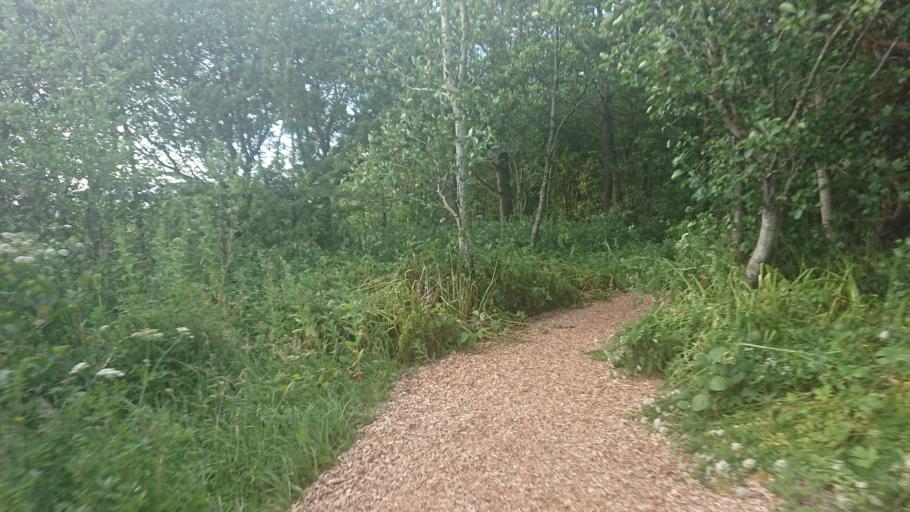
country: GB
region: England
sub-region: Lancashire
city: Galgate
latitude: 53.9983
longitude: -2.7881
